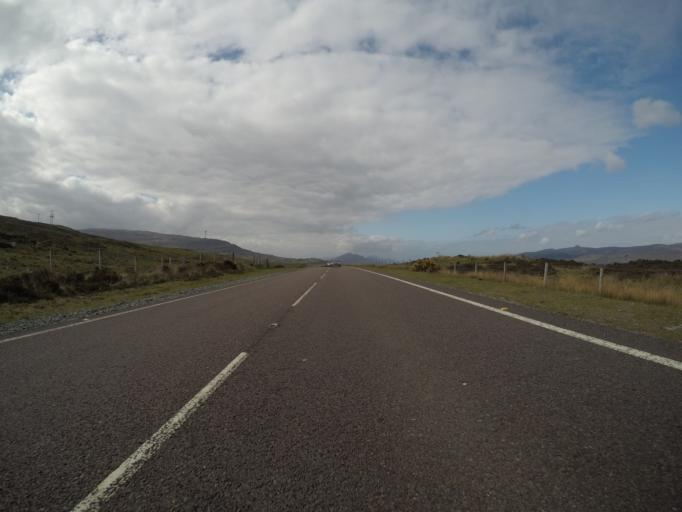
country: GB
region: Scotland
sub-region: Highland
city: Portree
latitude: 57.3065
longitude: -6.0917
